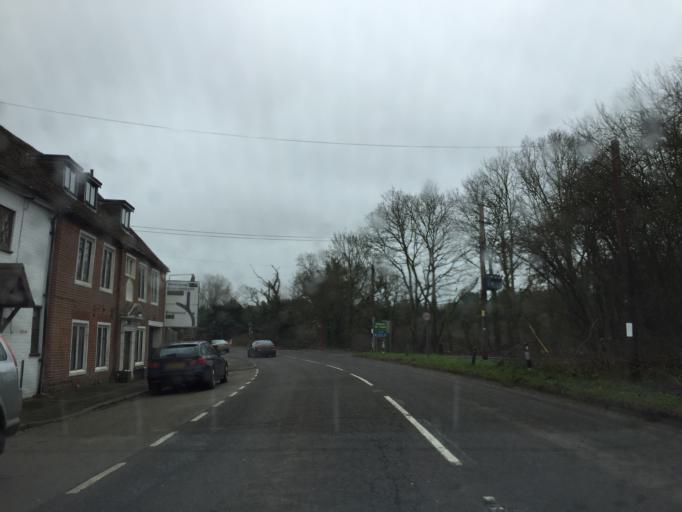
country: GB
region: England
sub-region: Hampshire
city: Ringwood
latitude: 50.8446
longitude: -1.8070
